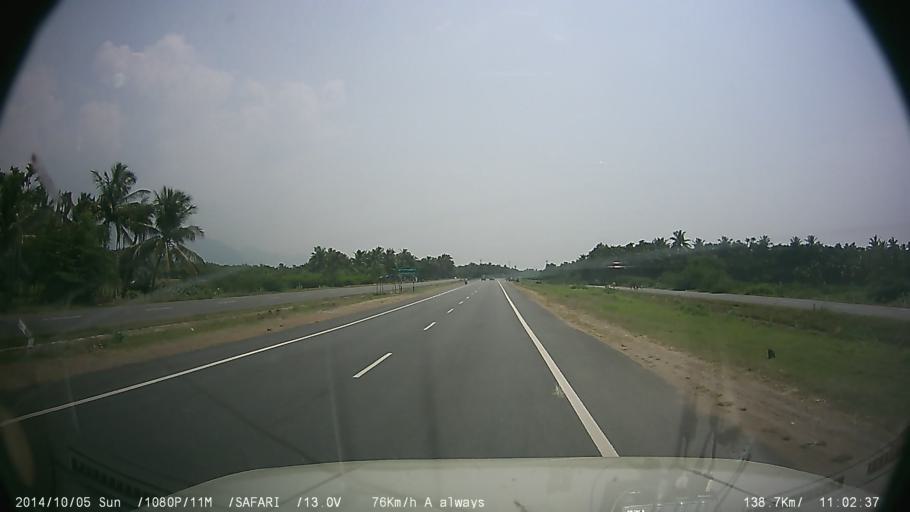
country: IN
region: Tamil Nadu
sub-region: Salem
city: Attur
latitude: 11.6139
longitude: 78.5752
